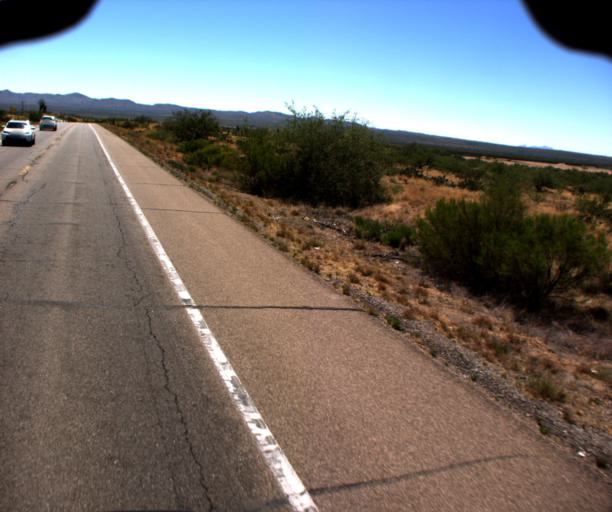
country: US
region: Arizona
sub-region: Pima County
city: Catalina
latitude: 32.5960
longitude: -110.8829
